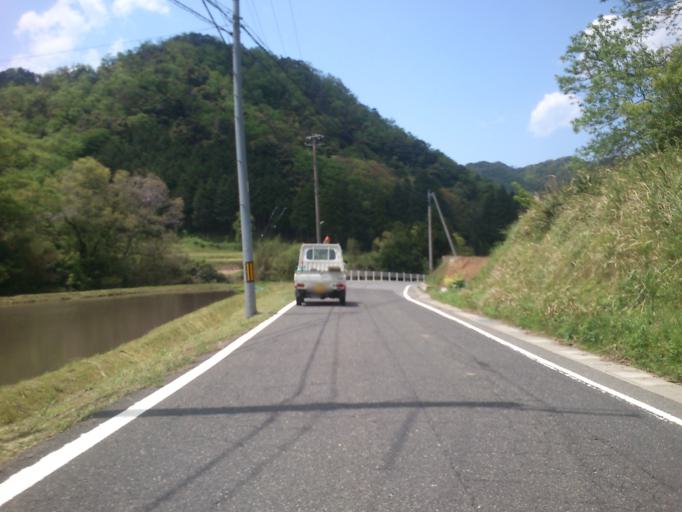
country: JP
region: Kyoto
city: Miyazu
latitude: 35.6866
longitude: 135.1513
